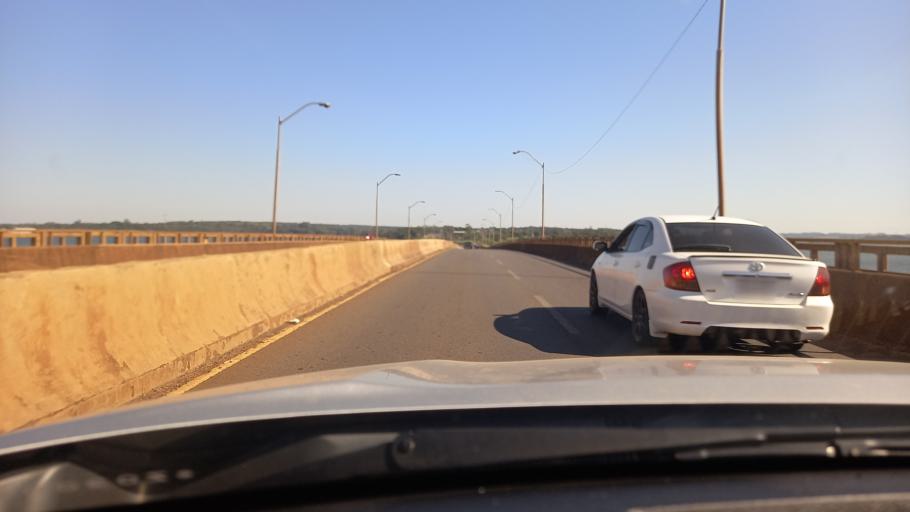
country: PY
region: Itapua
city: Encarnacion
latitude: -27.2999
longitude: -55.9018
